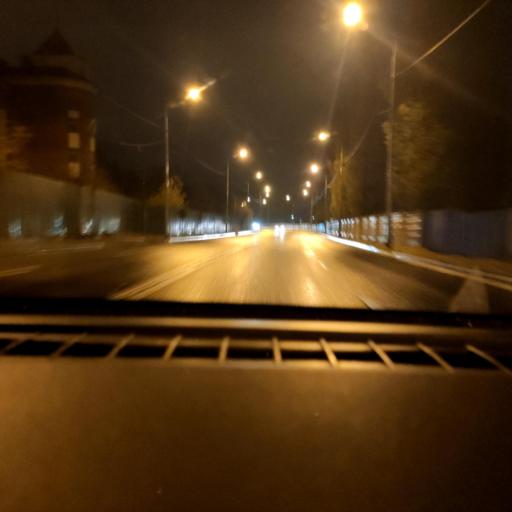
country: RU
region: Voronezj
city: Voronezh
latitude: 51.6861
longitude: 39.2293
